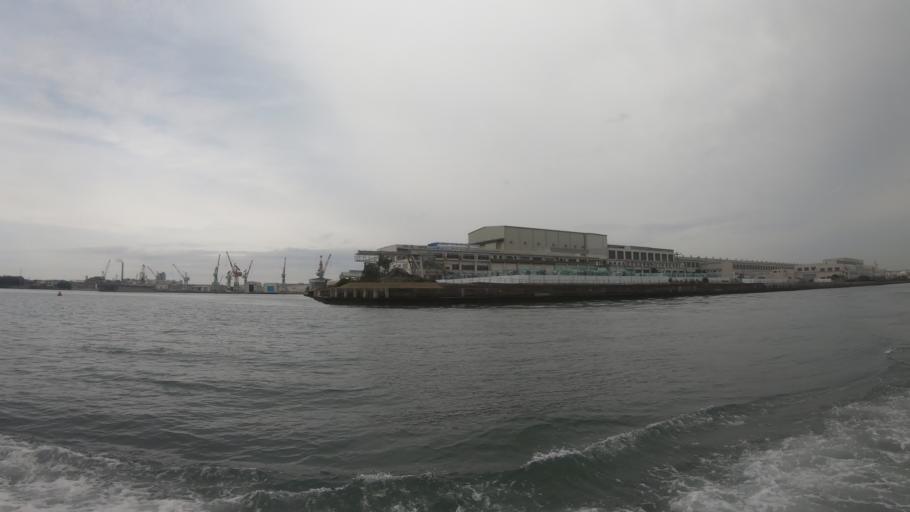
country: JP
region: Kanagawa
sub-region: Kawasaki-shi
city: Kawasaki
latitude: 35.4832
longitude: 139.6965
